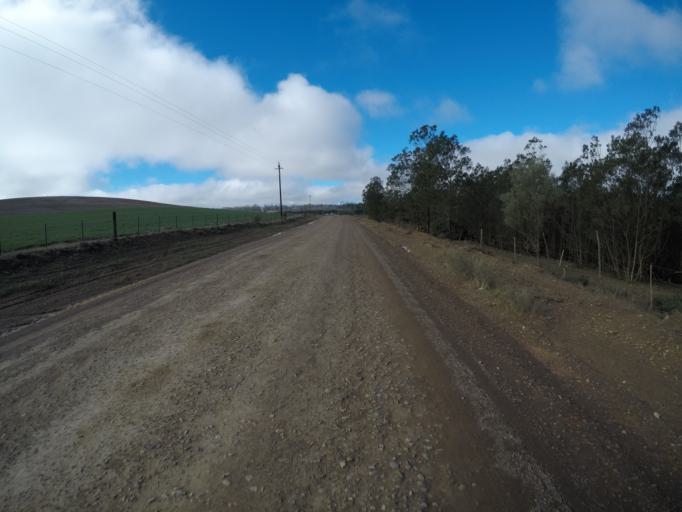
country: ZA
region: Western Cape
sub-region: Overberg District Municipality
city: Caledon
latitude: -34.1164
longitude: 19.7811
